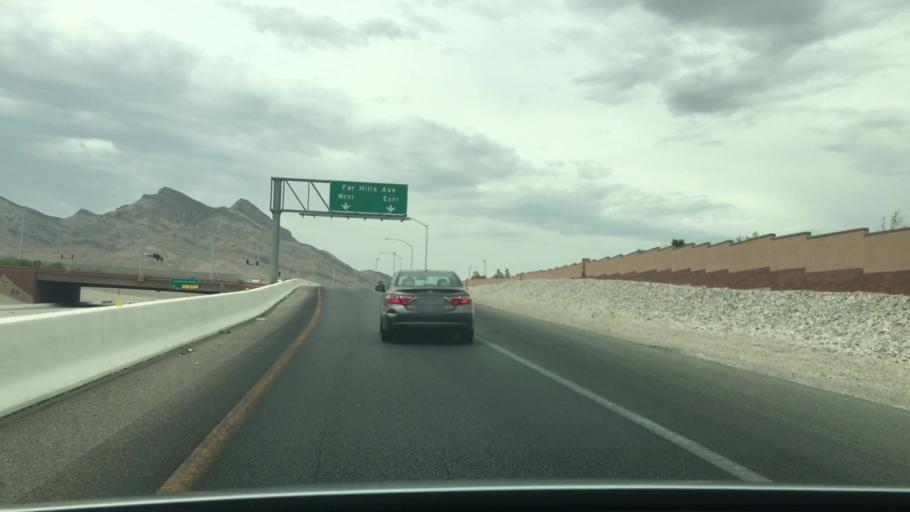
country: US
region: Nevada
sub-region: Clark County
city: Summerlin South
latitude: 36.1793
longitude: -115.3398
